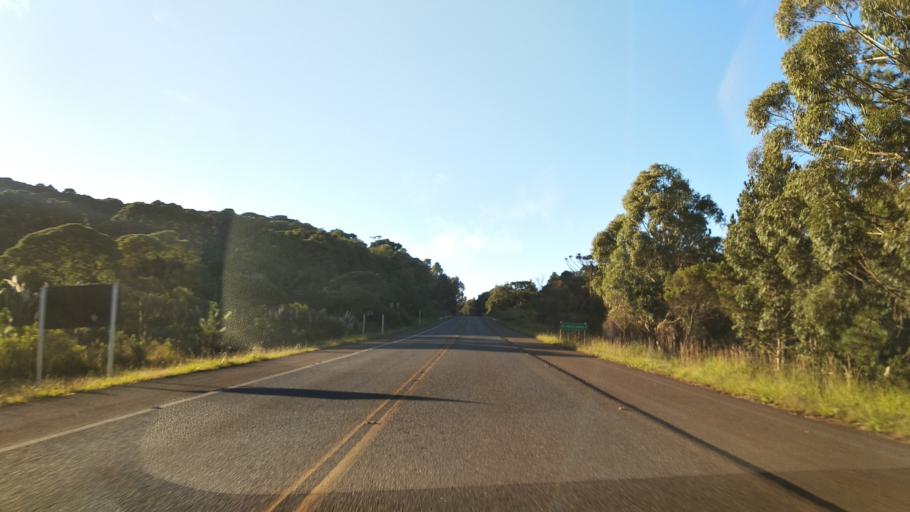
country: BR
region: Santa Catarina
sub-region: Correia Pinto
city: Correia Pinto
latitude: -27.6285
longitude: -50.6221
